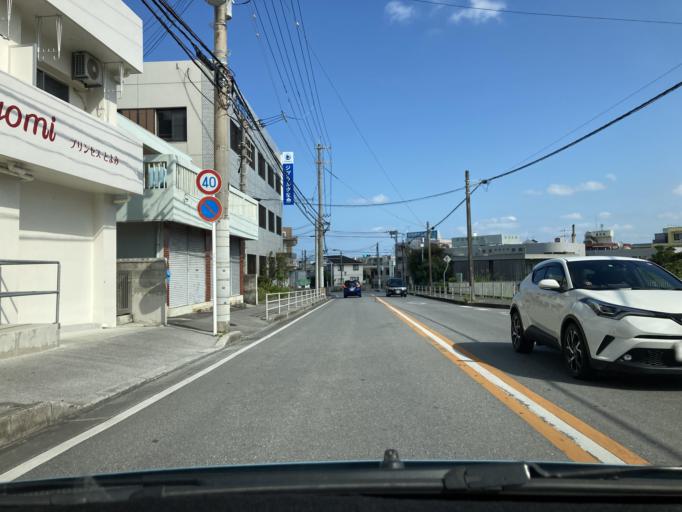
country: JP
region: Okinawa
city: Tomigusuku
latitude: 26.1884
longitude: 127.6806
